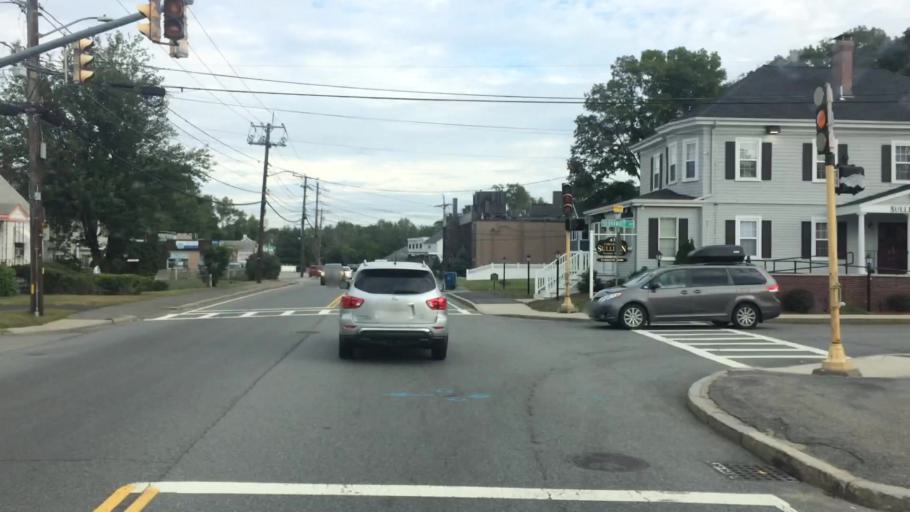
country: US
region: Massachusetts
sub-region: Middlesex County
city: Burlington
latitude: 42.4923
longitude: -71.1754
